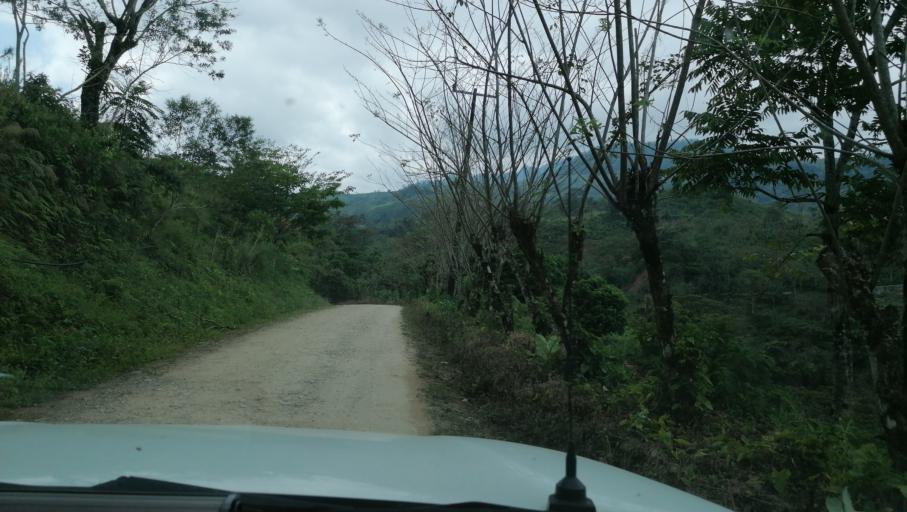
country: MX
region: Chiapas
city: Ocotepec
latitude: 17.2766
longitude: -93.2303
